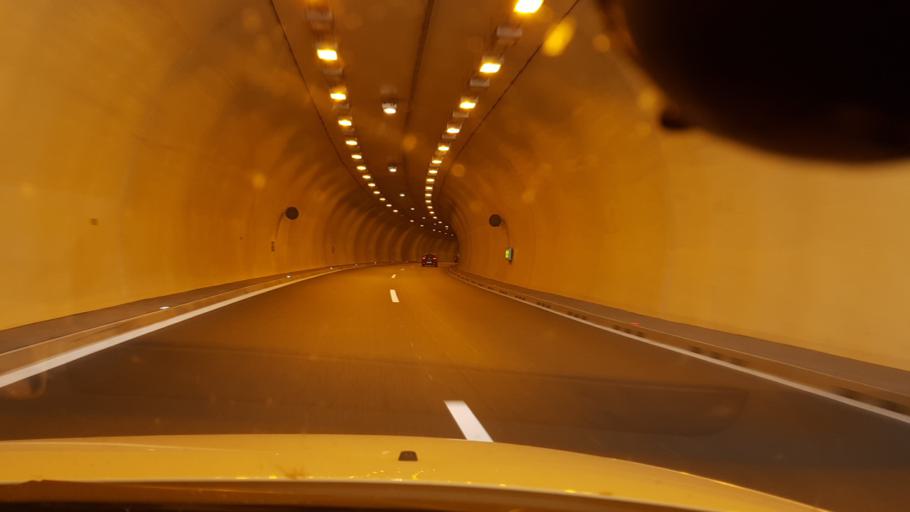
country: AT
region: Styria
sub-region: Politischer Bezirk Leoben
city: Leoben
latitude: 47.3710
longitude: 15.1042
